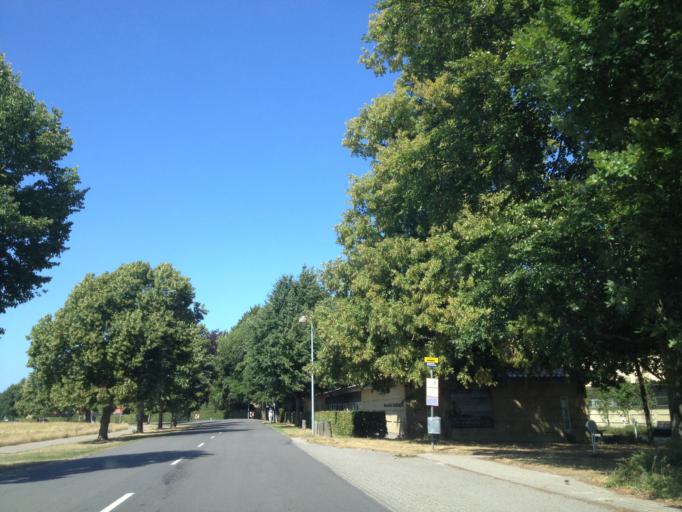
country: DK
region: Capital Region
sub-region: Fredensborg Kommune
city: Niva
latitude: 55.9266
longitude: 12.5104
